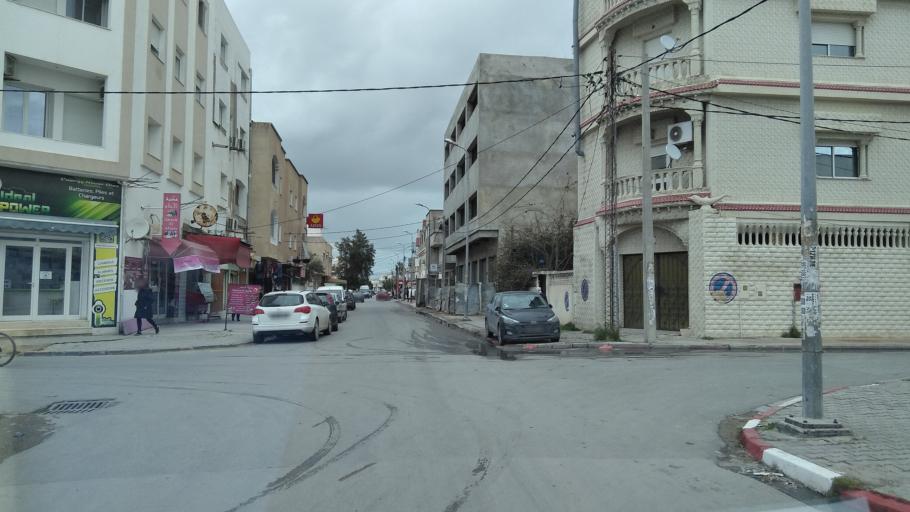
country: TN
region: Bin 'Arus
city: Ben Arous
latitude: 36.7571
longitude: 10.2230
